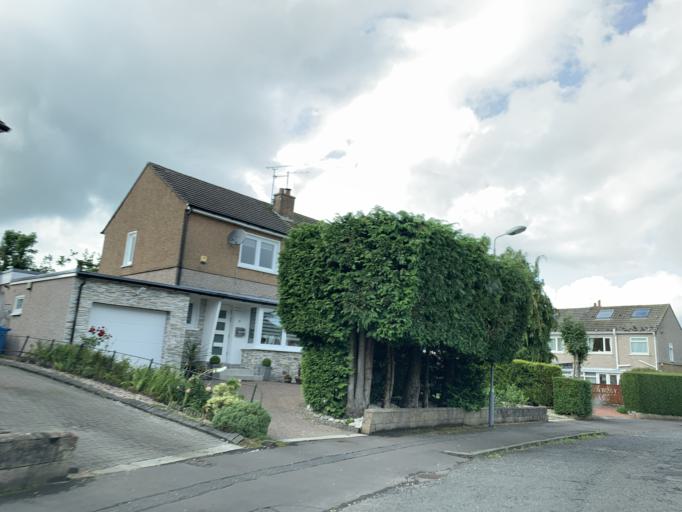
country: GB
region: Scotland
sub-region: East Renfrewshire
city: Newton Mearns
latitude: 55.7831
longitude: -4.3251
